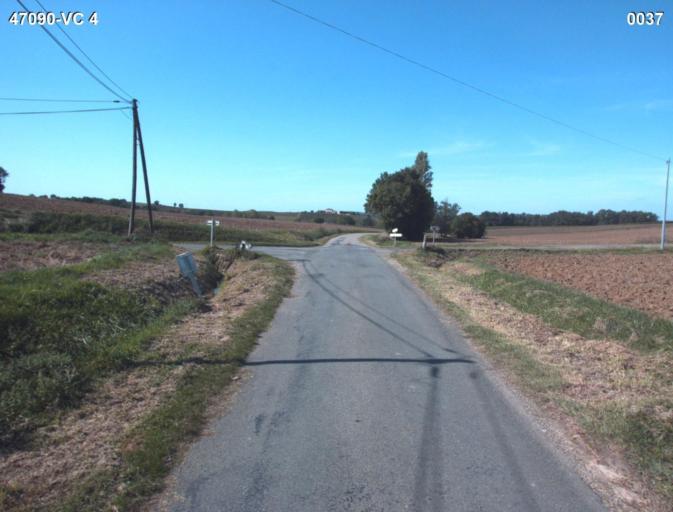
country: FR
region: Aquitaine
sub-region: Departement du Lot-et-Garonne
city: Vianne
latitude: 44.1784
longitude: 0.3436
